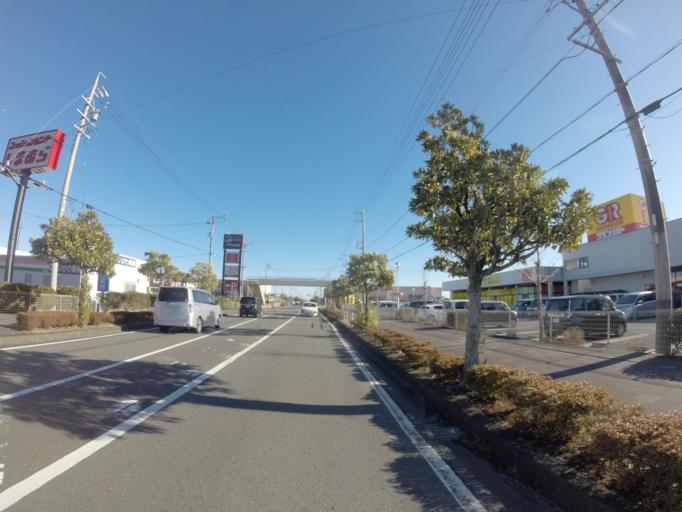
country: JP
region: Shizuoka
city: Fujieda
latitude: 34.8103
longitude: 138.2752
